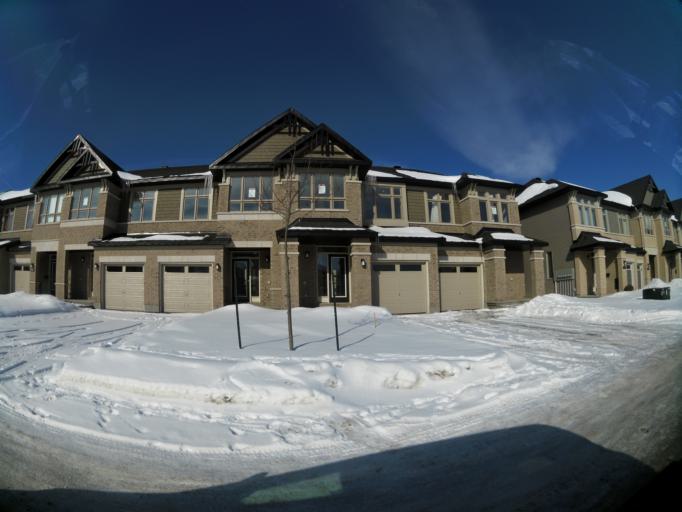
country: CA
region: Ontario
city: Ottawa
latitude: 45.4360
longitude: -75.5122
